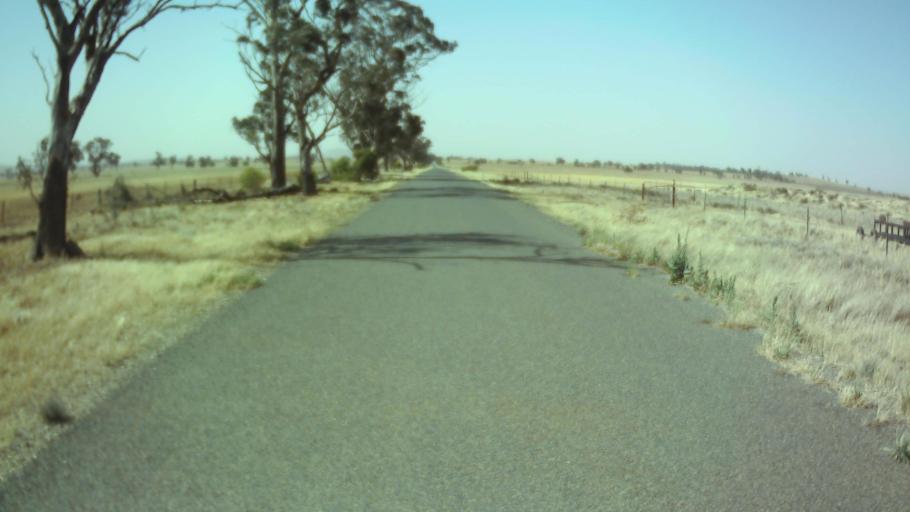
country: AU
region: New South Wales
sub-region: Weddin
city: Grenfell
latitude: -33.8764
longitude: 147.9253
